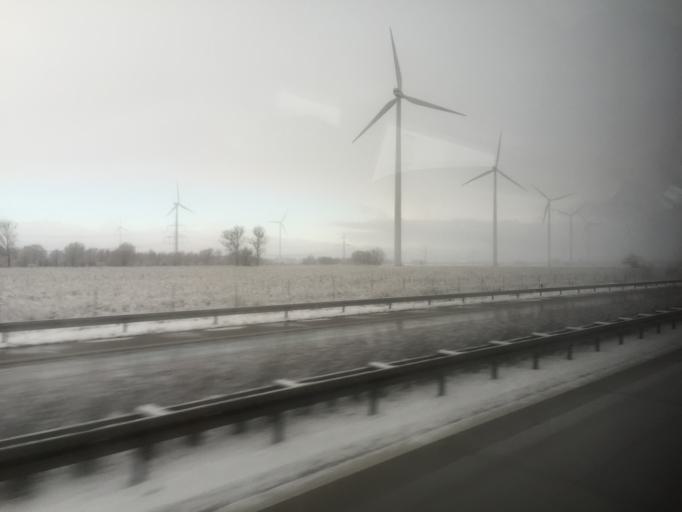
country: DE
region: Brandenburg
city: Kasel-Golzig
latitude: 51.9820
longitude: 13.7373
